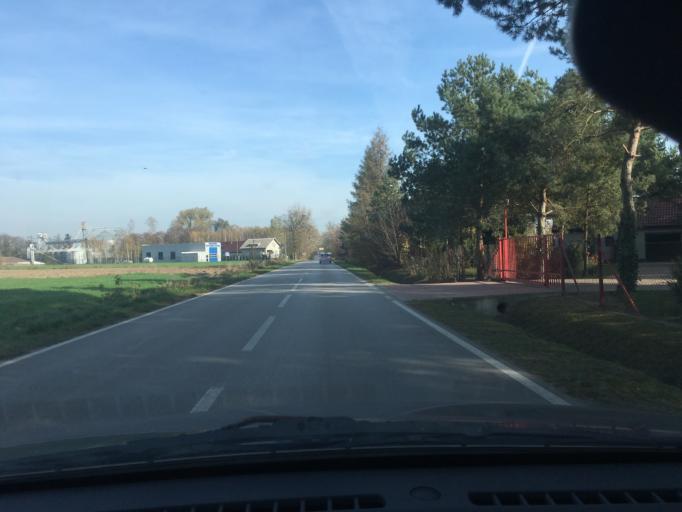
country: PL
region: Masovian Voivodeship
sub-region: Powiat plocki
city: Bodzanow
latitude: 52.4903
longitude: 20.0250
